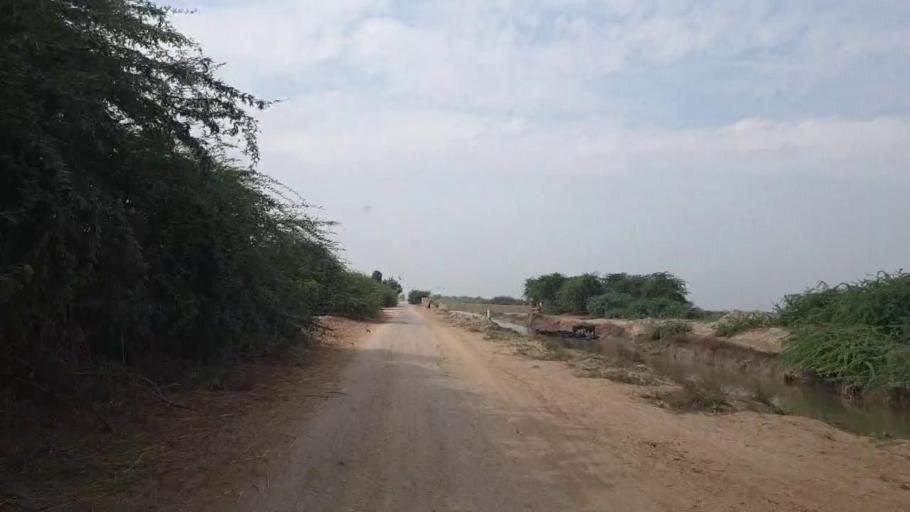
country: PK
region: Sindh
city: Kario
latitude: 24.6226
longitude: 68.5802
